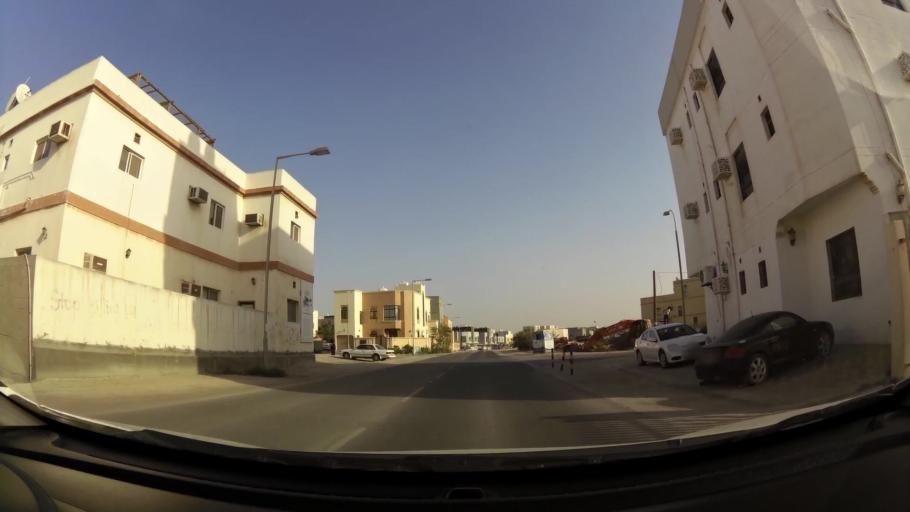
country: BH
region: Manama
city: Jidd Hafs
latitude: 26.2114
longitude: 50.5015
